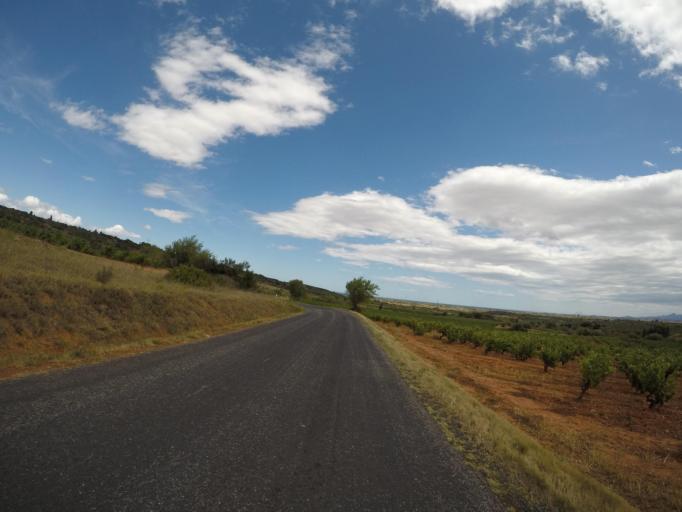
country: FR
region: Languedoc-Roussillon
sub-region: Departement des Pyrenees-Orientales
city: Baixas
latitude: 42.7493
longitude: 2.7825
